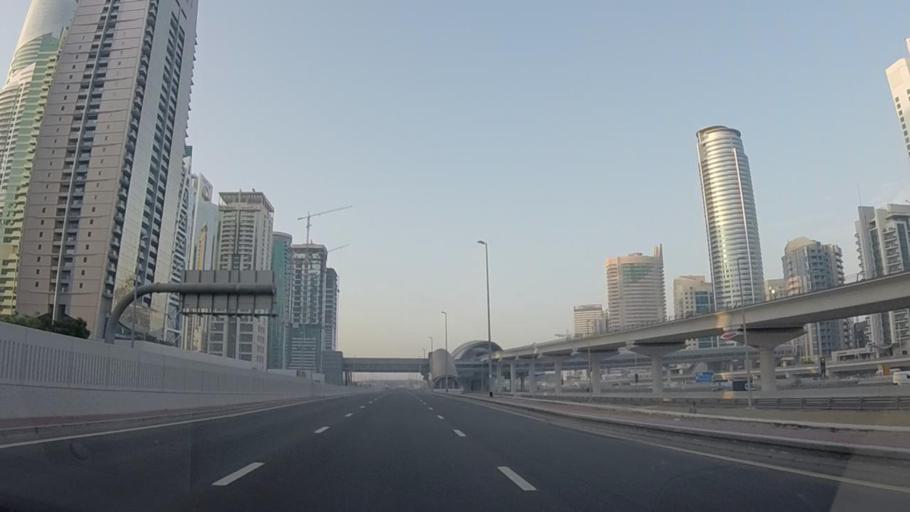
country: AE
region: Dubai
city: Dubai
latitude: 25.0730
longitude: 55.1411
